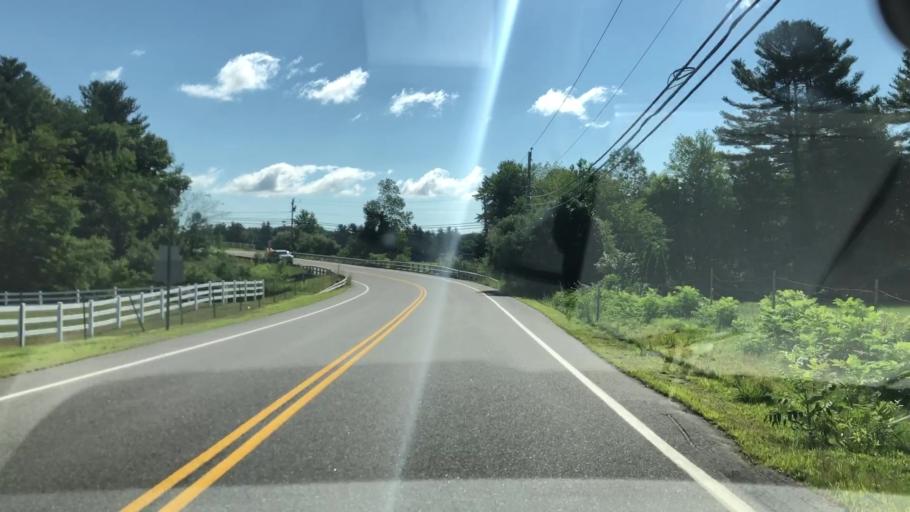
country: US
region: New Hampshire
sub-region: Hillsborough County
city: Milford
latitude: 42.8357
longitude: -71.6105
